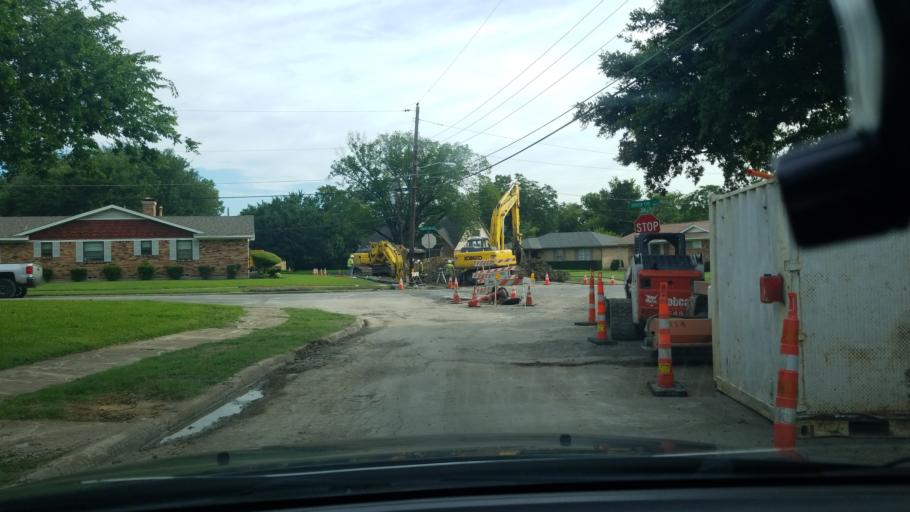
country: US
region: Texas
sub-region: Dallas County
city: Balch Springs
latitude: 32.7541
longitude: -96.6675
